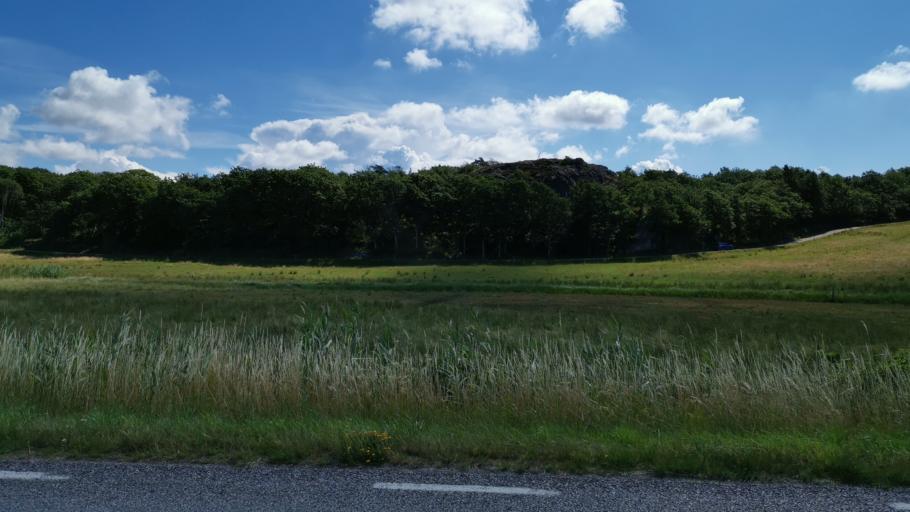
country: SE
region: Vaestra Goetaland
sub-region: Lysekils Kommun
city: Lysekil
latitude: 58.2255
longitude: 11.4580
